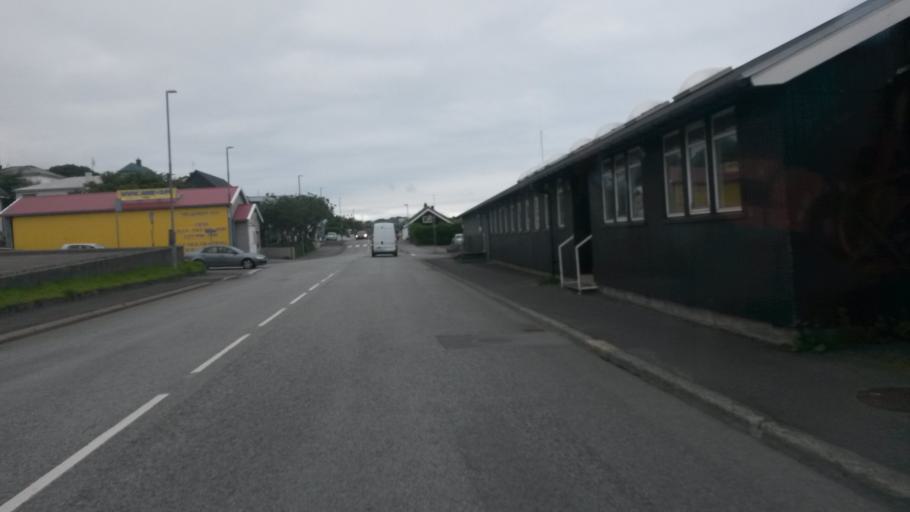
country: FO
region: Streymoy
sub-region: Torshavn
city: Torshavn
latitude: 62.0032
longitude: -6.7774
